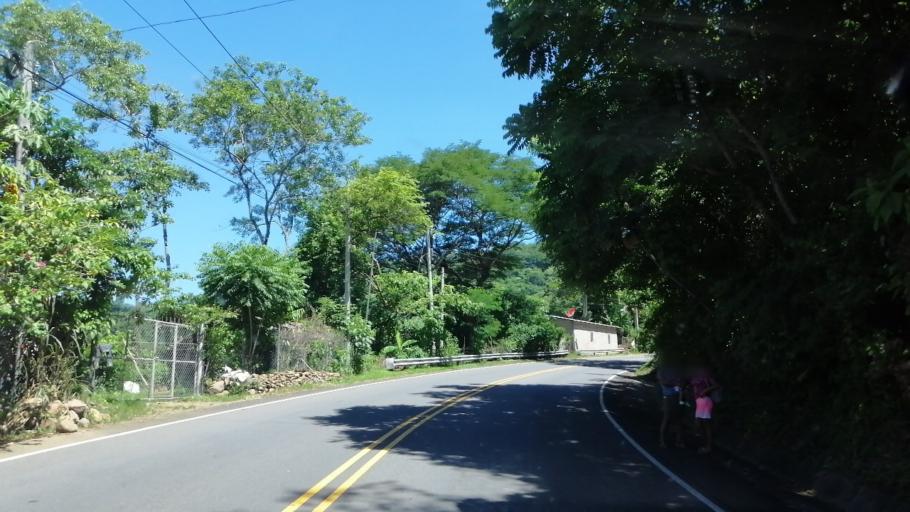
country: SV
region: Morazan
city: Cacaopera
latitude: 13.7965
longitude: -88.1472
